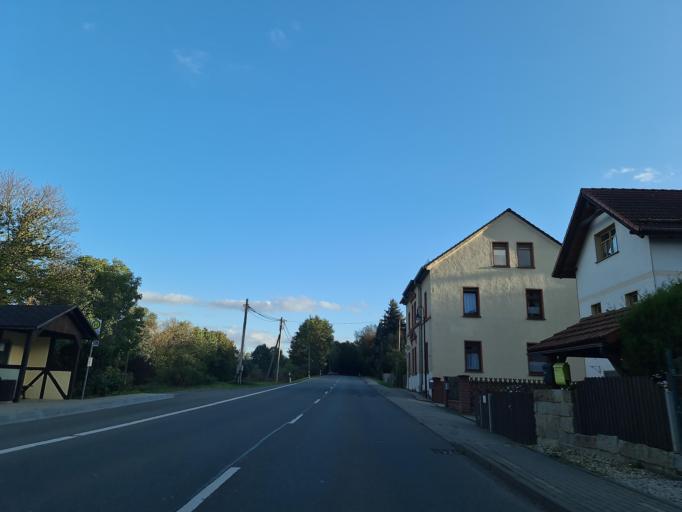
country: DE
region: Thuringia
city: Crimla
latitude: 50.8139
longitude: 12.0738
